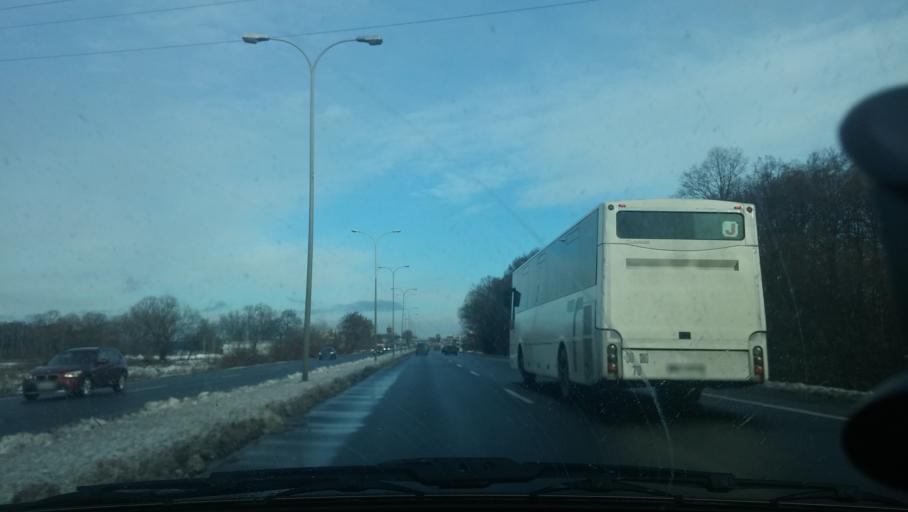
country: PL
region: Masovian Voivodeship
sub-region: Powiat wolominski
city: Zabki
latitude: 52.2958
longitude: 21.0826
